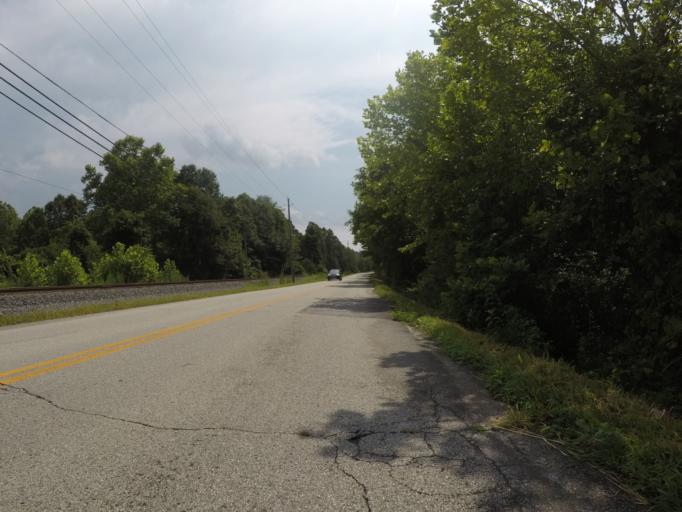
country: US
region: Kentucky
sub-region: Boyd County
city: Ironville
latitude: 38.4459
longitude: -82.6972
